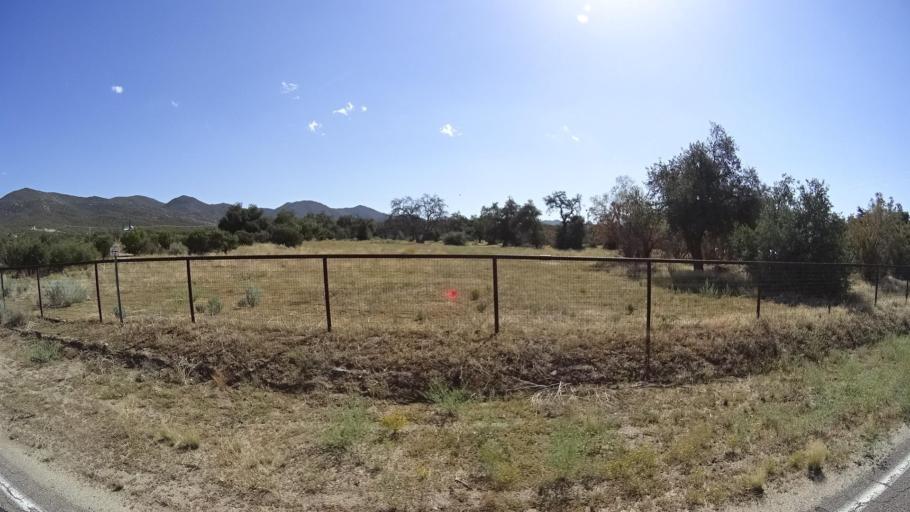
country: US
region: California
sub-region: Riverside County
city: Anza
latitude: 33.3824
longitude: -116.6521
